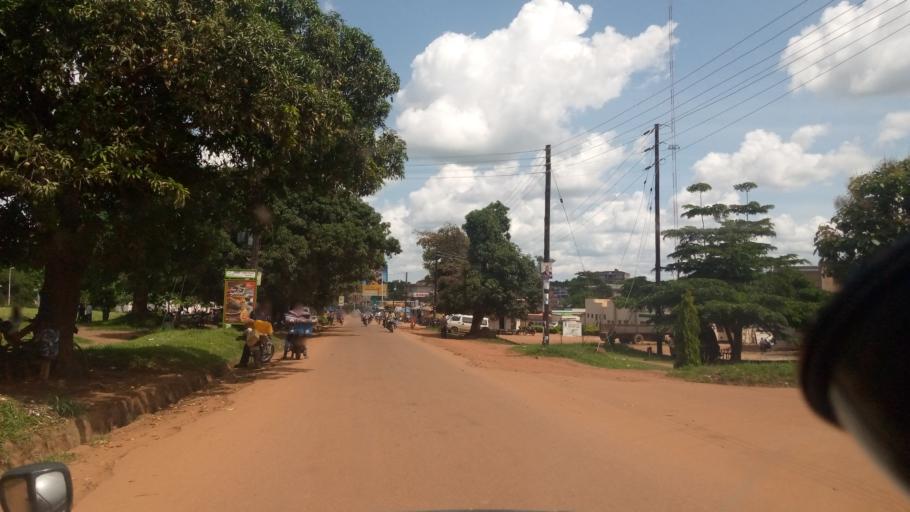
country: UG
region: Northern Region
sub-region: Lira District
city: Lira
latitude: 2.2475
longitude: 32.8986
